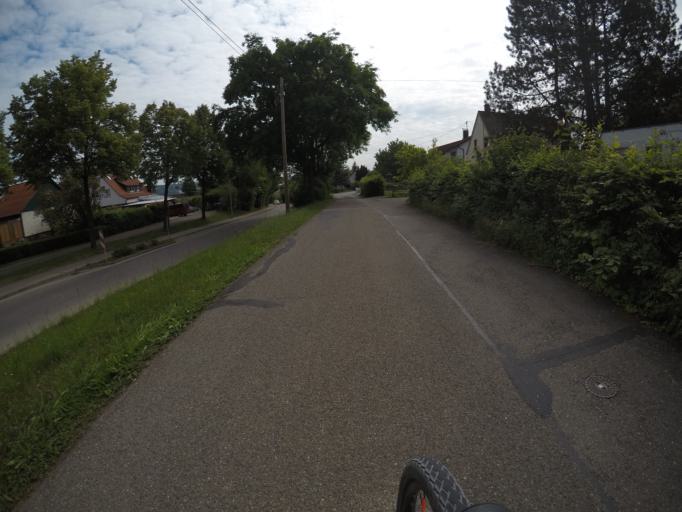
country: DE
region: Baden-Wuerttemberg
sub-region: Regierungsbezirk Stuttgart
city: Kirchheim unter Teck
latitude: 48.6453
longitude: 9.4193
